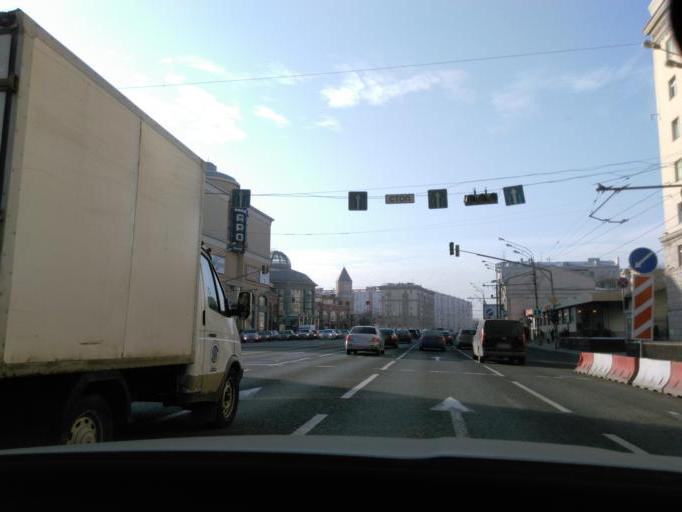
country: RU
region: Moscow
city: Taganskiy
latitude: 55.7589
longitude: 37.6577
